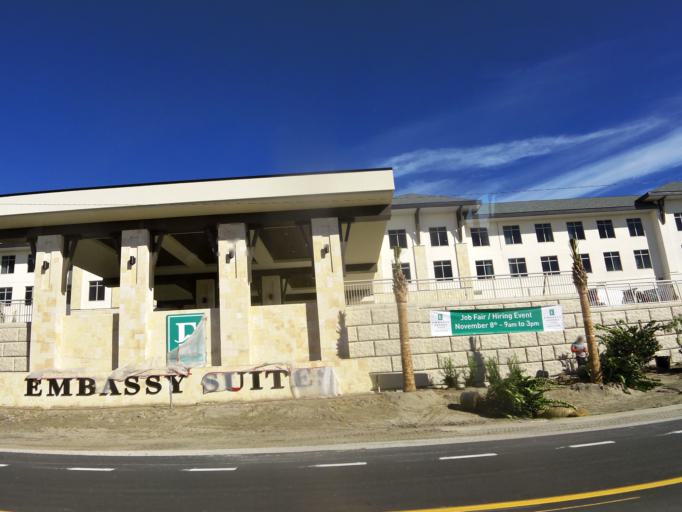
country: US
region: Florida
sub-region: Saint Johns County
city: Saint Augustine Beach
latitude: 29.8584
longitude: -81.2672
